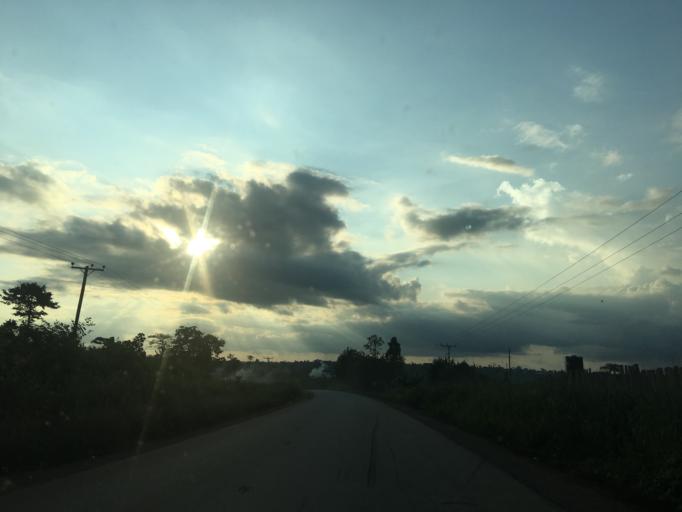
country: GH
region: Western
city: Bibiani
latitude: 6.6318
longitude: -2.4185
